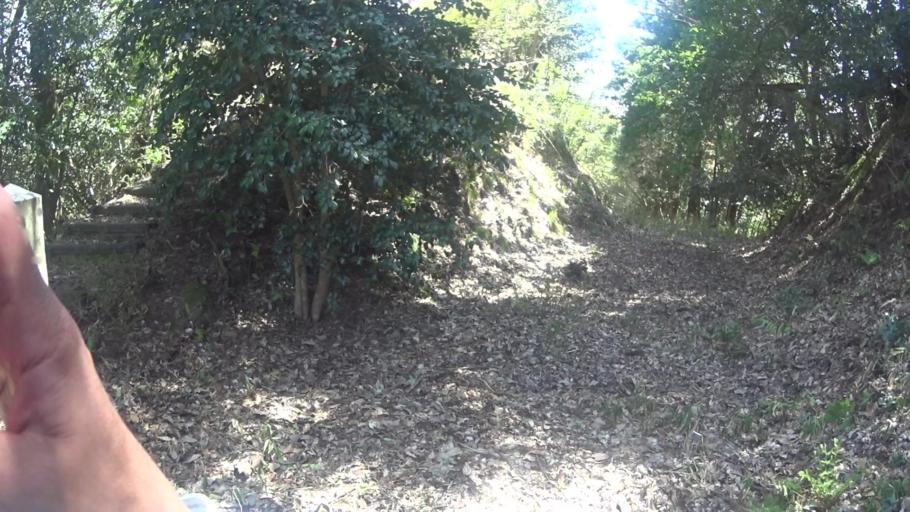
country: JP
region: Kyoto
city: Miyazu
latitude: 35.5645
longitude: 135.1372
